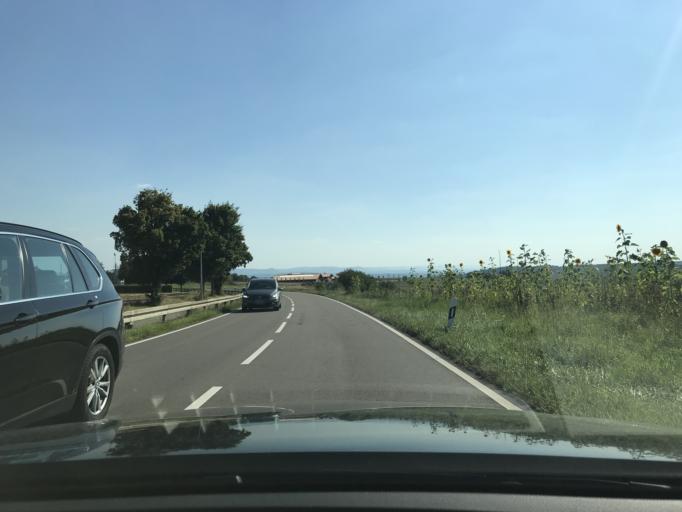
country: DE
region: Baden-Wuerttemberg
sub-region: Regierungsbezirk Stuttgart
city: Baltmannsweiler
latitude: 48.7479
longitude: 9.4833
